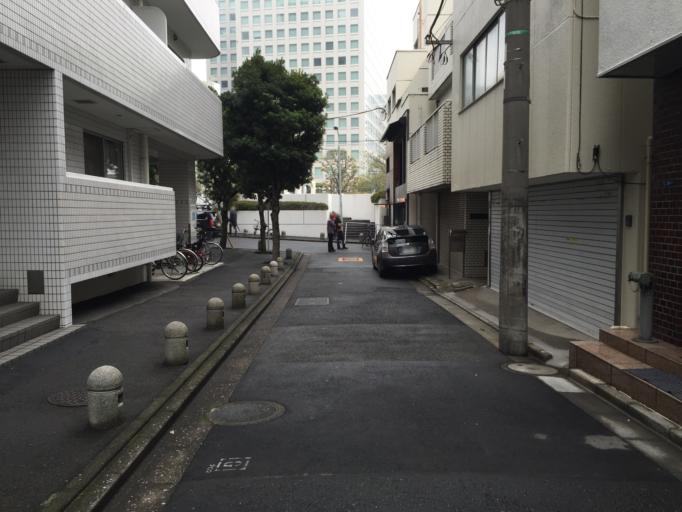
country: JP
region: Tokyo
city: Tokyo
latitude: 35.6769
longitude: 139.7865
